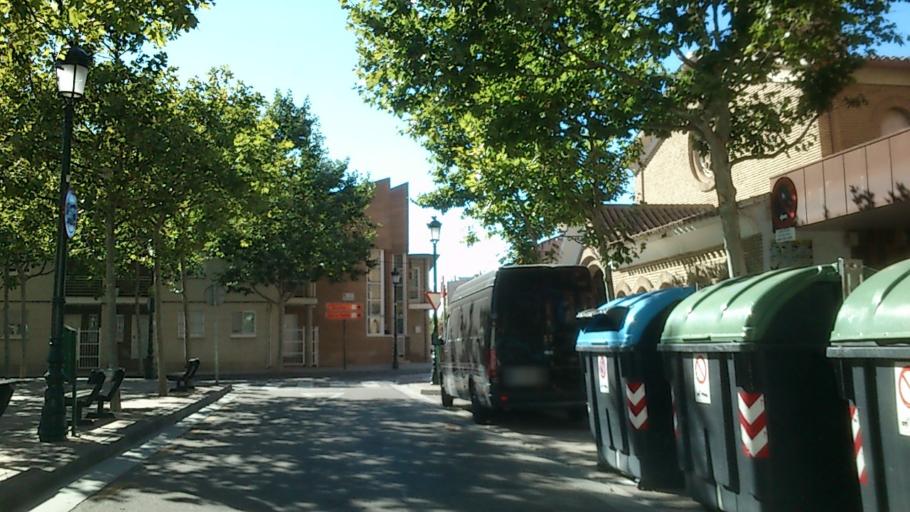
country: ES
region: Aragon
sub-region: Provincia de Zaragoza
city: Zaragoza
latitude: 41.6672
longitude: -0.8313
